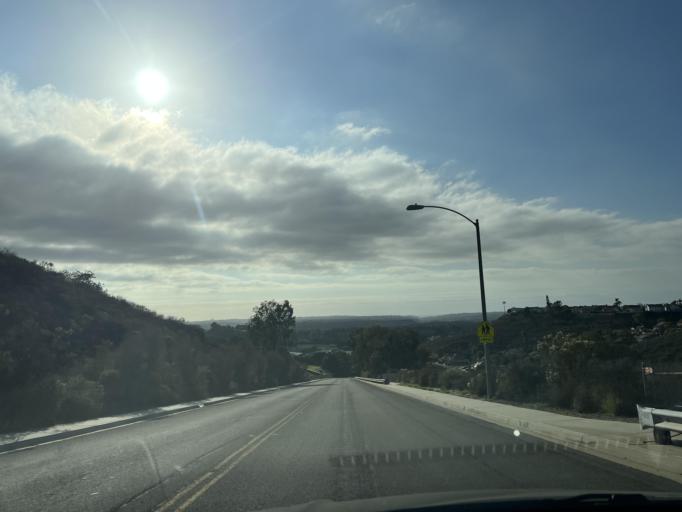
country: US
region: California
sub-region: San Diego County
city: Fairbanks Ranch
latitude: 32.9721
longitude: -117.1208
